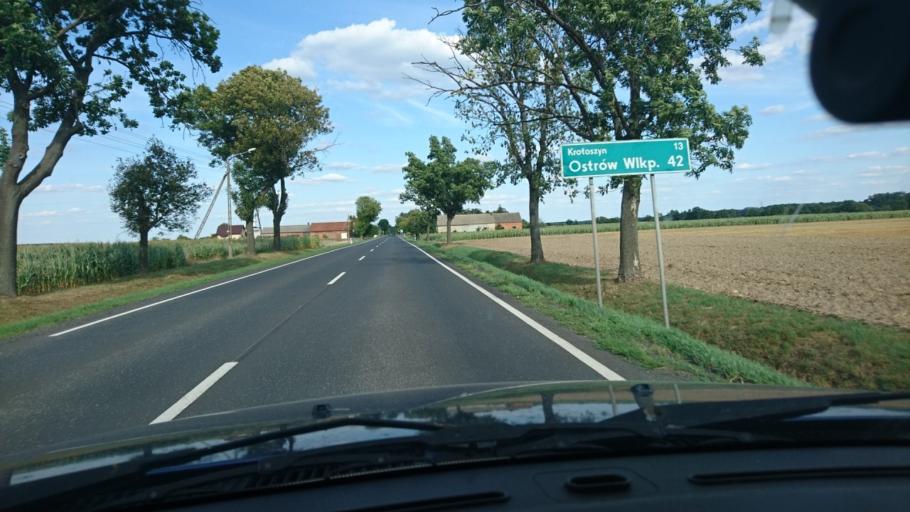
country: PL
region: Greater Poland Voivodeship
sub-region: Powiat krotoszynski
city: Kobylin
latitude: 51.7298
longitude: 17.2782
